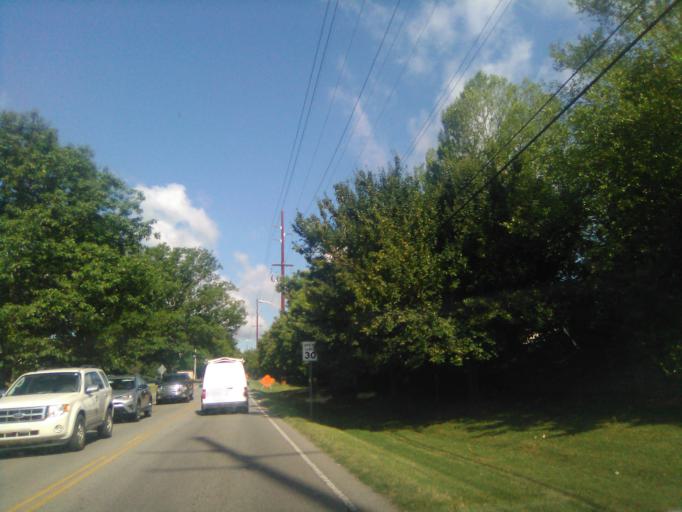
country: US
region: Tennessee
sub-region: Davidson County
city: Belle Meade
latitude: 36.1153
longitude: -86.8631
